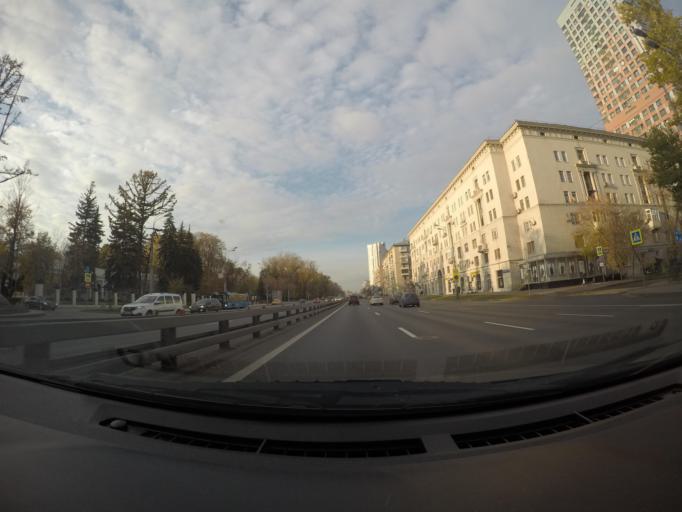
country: RU
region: Moskovskaya
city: Levoberezhnyy
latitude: 55.8551
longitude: 37.4704
